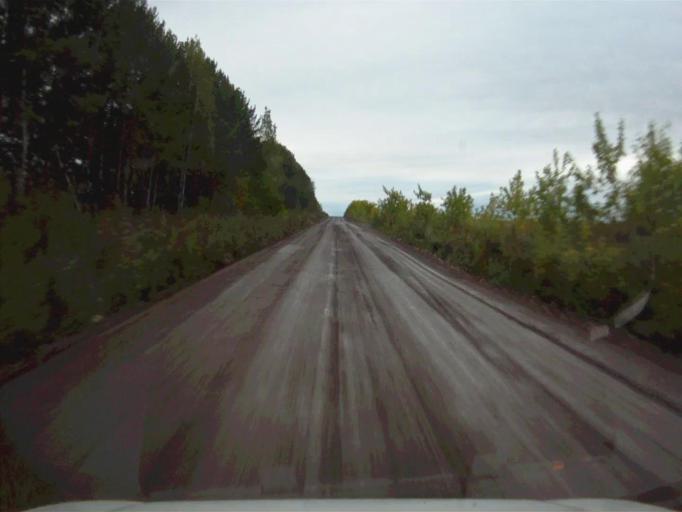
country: RU
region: Sverdlovsk
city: Mikhaylovsk
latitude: 56.1536
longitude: 59.2635
